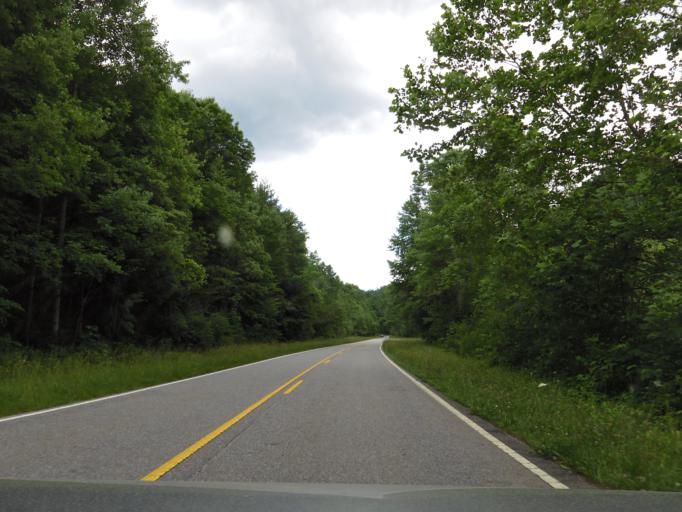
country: US
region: North Carolina
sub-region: Graham County
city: Robbinsville
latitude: 35.4092
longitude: -83.8865
